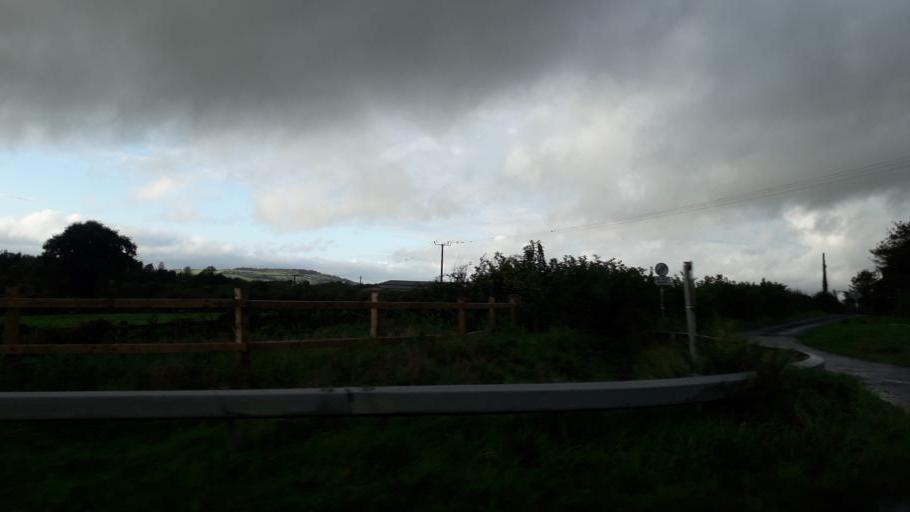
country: IE
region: Leinster
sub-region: An Longfort
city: Lanesborough
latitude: 53.7653
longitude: -8.0634
